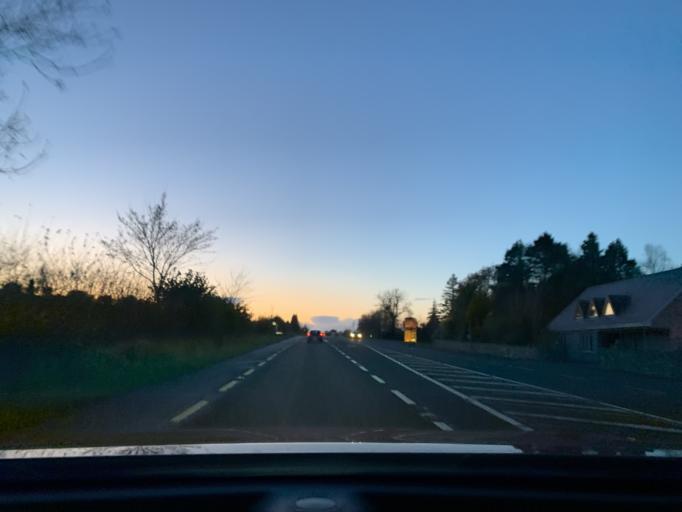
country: IE
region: Connaught
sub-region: Roscommon
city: Boyle
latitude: 53.9698
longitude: -8.2446
